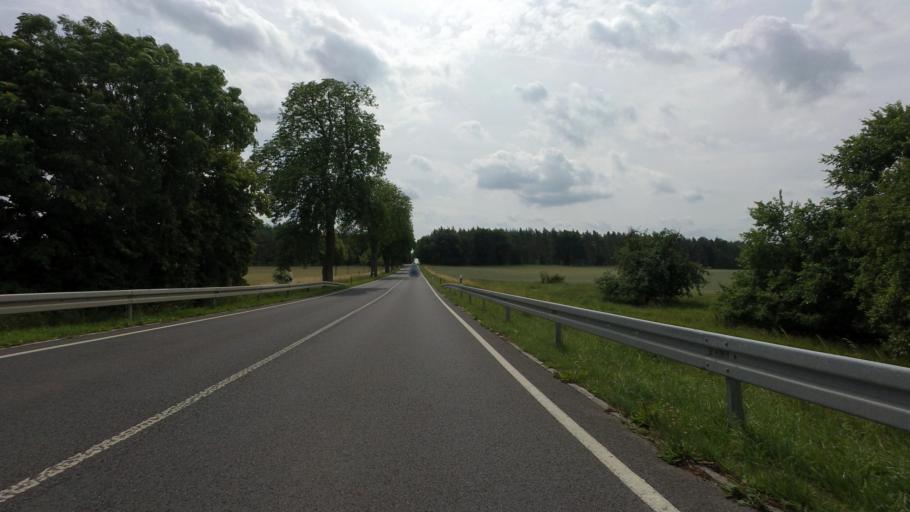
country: DE
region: Brandenburg
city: Angermunde
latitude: 53.0568
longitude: 13.9745
